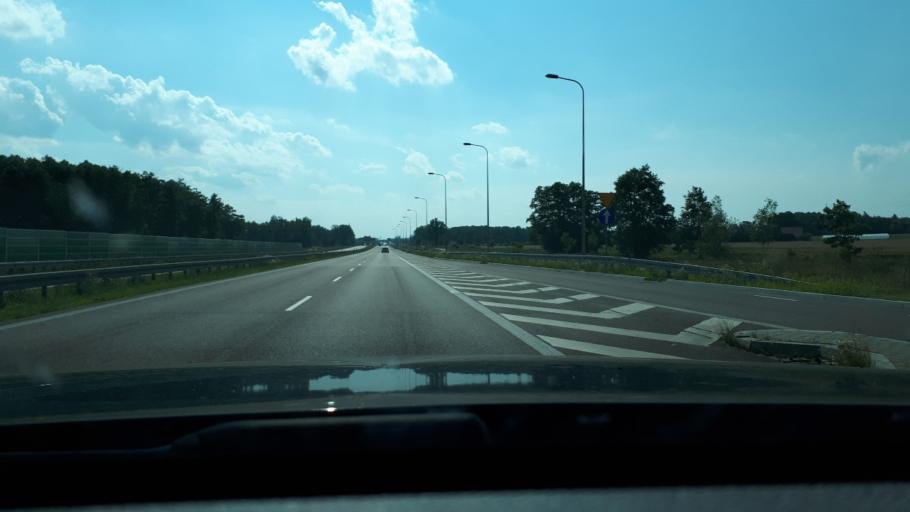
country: PL
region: Podlasie
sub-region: Powiat bialostocki
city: Choroszcz
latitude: 53.1588
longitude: 22.8874
